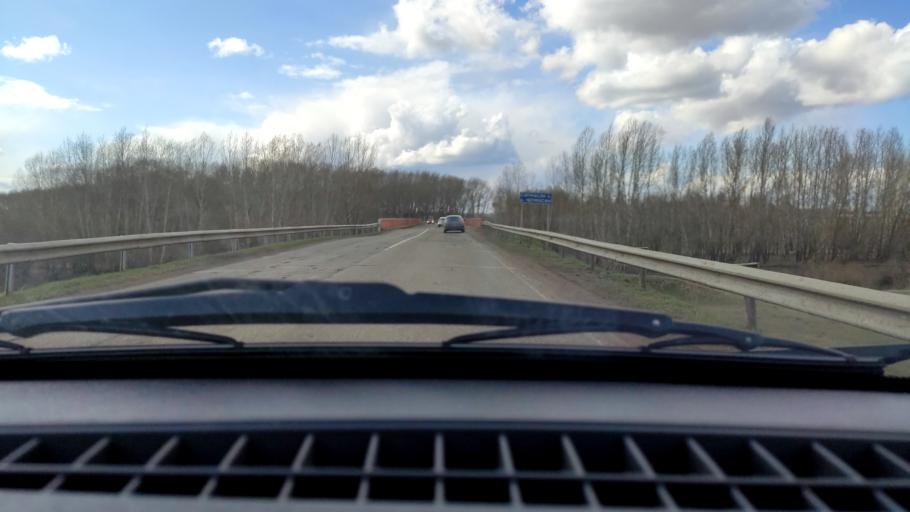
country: RU
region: Bashkortostan
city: Alekseyevka
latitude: 55.0776
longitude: 55.0714
